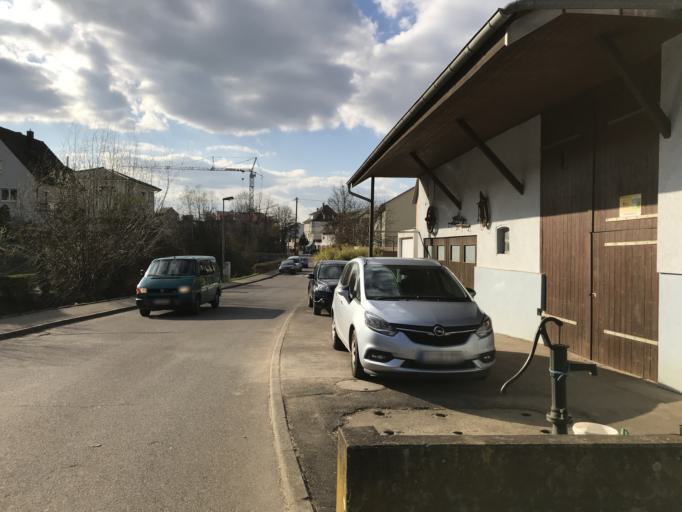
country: DE
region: Baden-Wuerttemberg
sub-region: Regierungsbezirk Stuttgart
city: Oberboihingen
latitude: 48.6478
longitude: 9.3725
